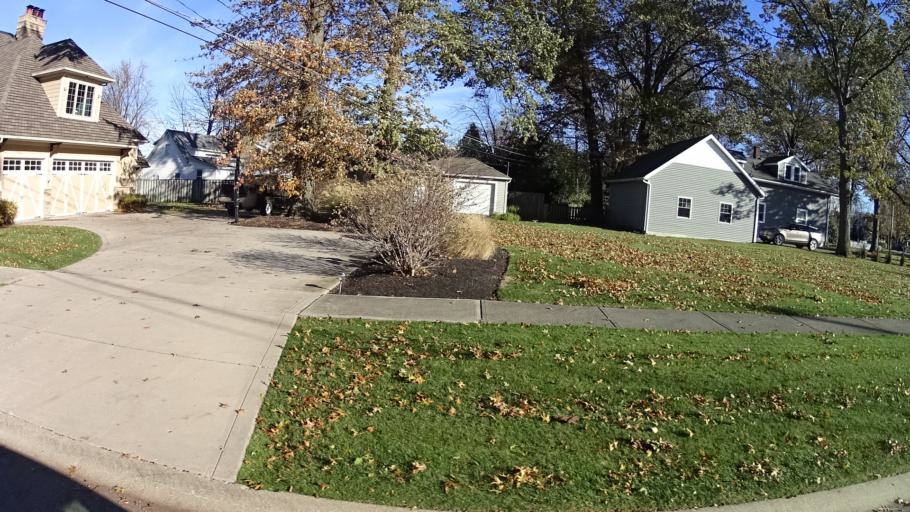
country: US
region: Ohio
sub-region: Lorain County
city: Avon Lake
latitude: 41.5111
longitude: -81.9880
